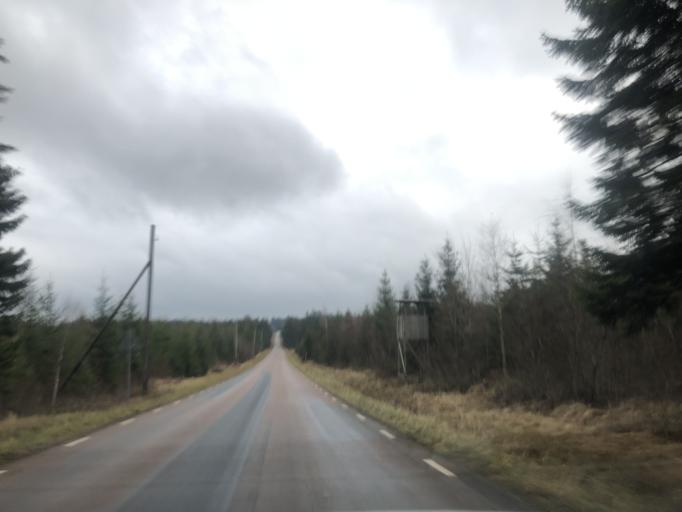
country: SE
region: Vaestra Goetaland
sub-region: Ulricehamns Kommun
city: Ulricehamn
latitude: 57.8288
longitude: 13.5033
